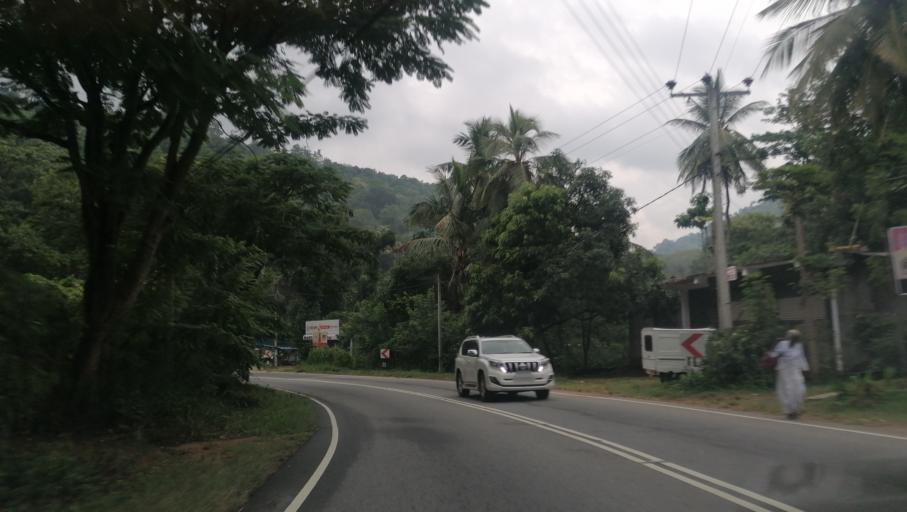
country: LK
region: Central
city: Kandy
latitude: 7.2470
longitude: 80.7246
